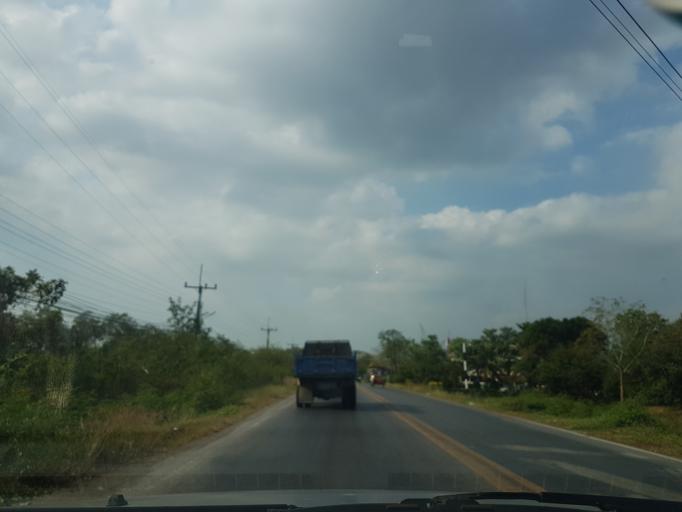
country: TH
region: Phra Nakhon Si Ayutthaya
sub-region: Amphoe Tha Ruea
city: Tha Ruea
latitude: 14.5534
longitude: 100.7247
